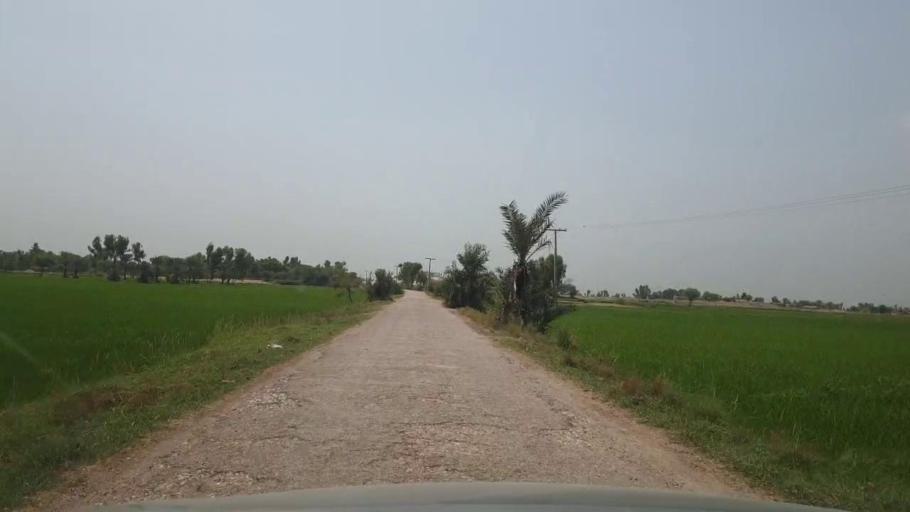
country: PK
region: Sindh
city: Garhi Yasin
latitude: 27.9314
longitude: 68.4010
